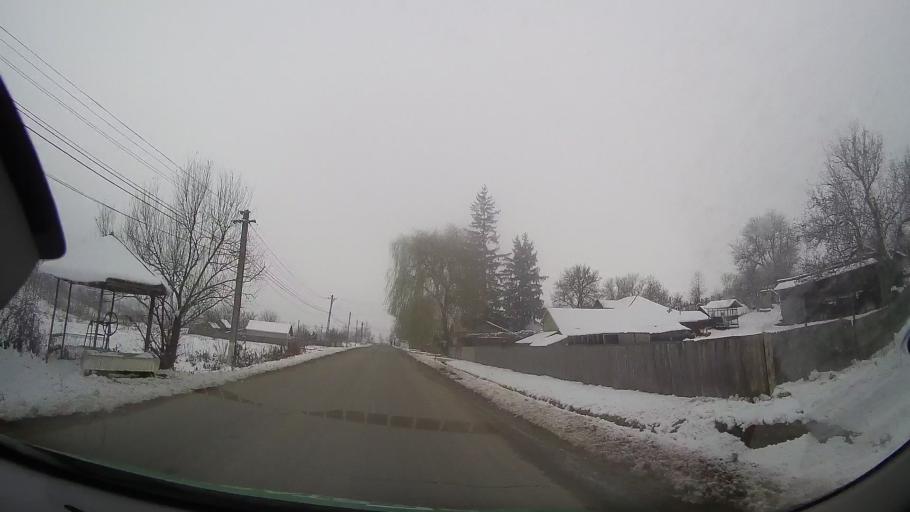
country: RO
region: Bacau
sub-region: Comuna Vultureni
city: Vultureni
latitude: 46.3998
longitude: 27.2732
